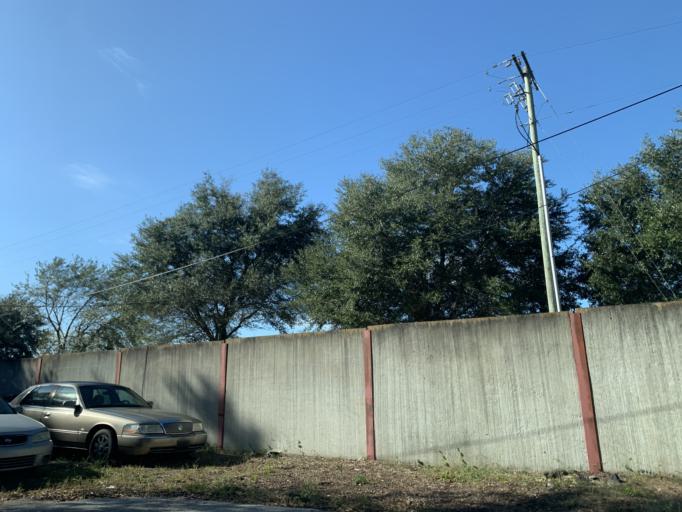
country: US
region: Florida
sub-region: Hillsborough County
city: Temple Terrace
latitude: 28.0348
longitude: -82.4139
